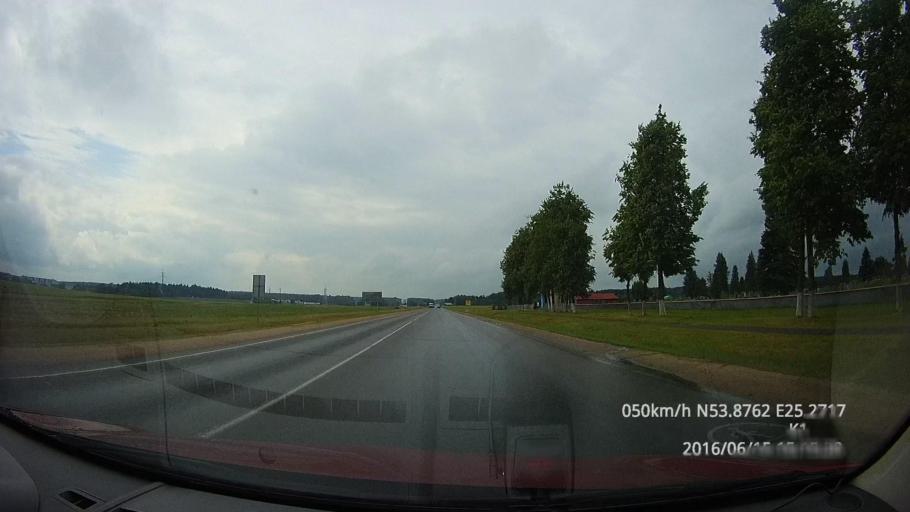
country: BY
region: Grodnenskaya
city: Lida
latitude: 53.8762
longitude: 25.2715
